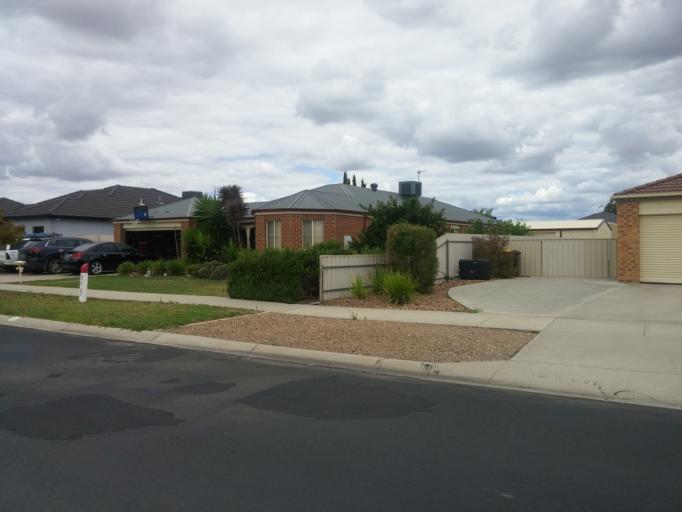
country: AU
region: Victoria
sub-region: Horsham
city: Horsham
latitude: -36.7270
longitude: 142.1997
